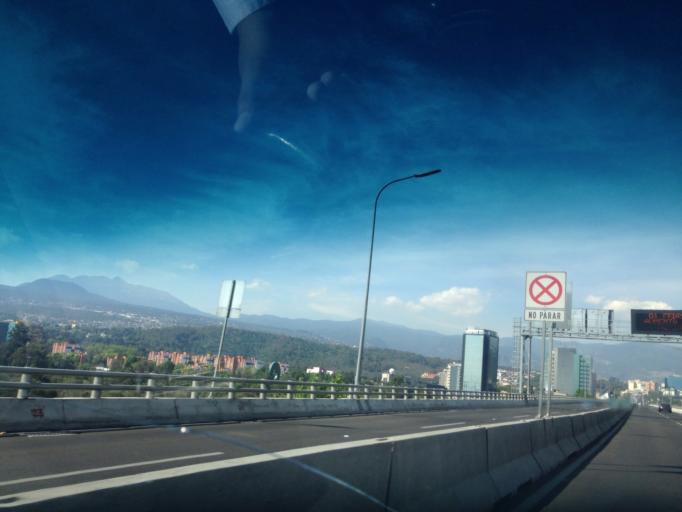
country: MX
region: Mexico City
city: Tlalpan
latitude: 19.3034
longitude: -99.1814
